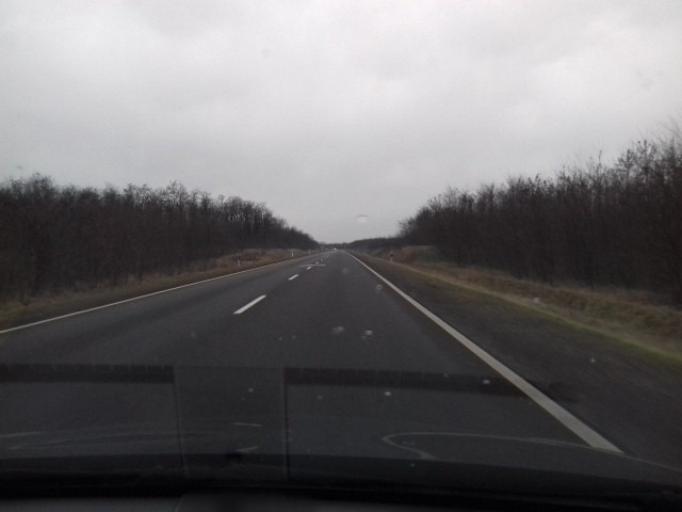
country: HU
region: Szabolcs-Szatmar-Bereg
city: Nyirpazony
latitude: 47.9992
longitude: 21.8337
